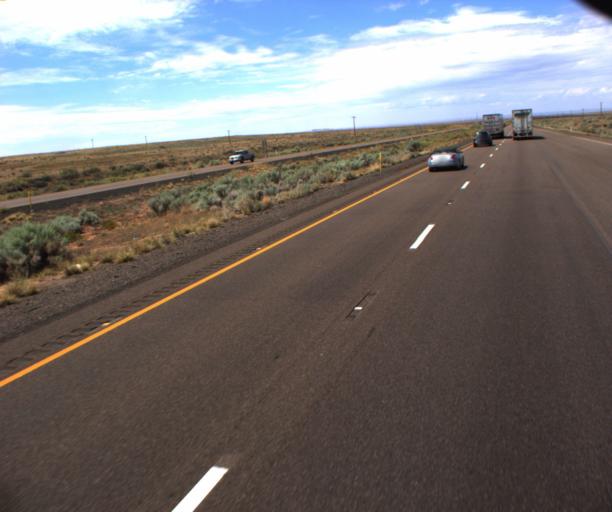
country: US
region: Arizona
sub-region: Navajo County
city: Holbrook
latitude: 35.0569
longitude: -109.7876
